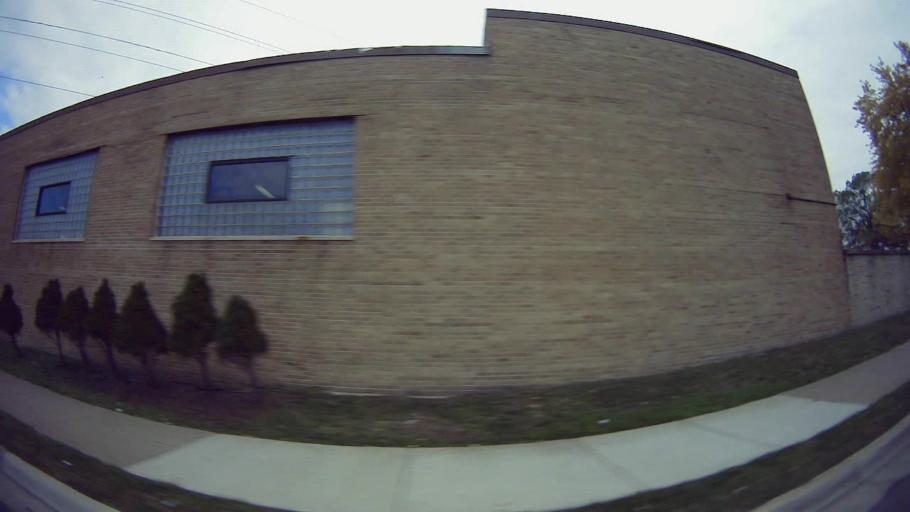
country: US
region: Michigan
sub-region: Wayne County
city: Dearborn
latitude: 42.3337
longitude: -83.1763
